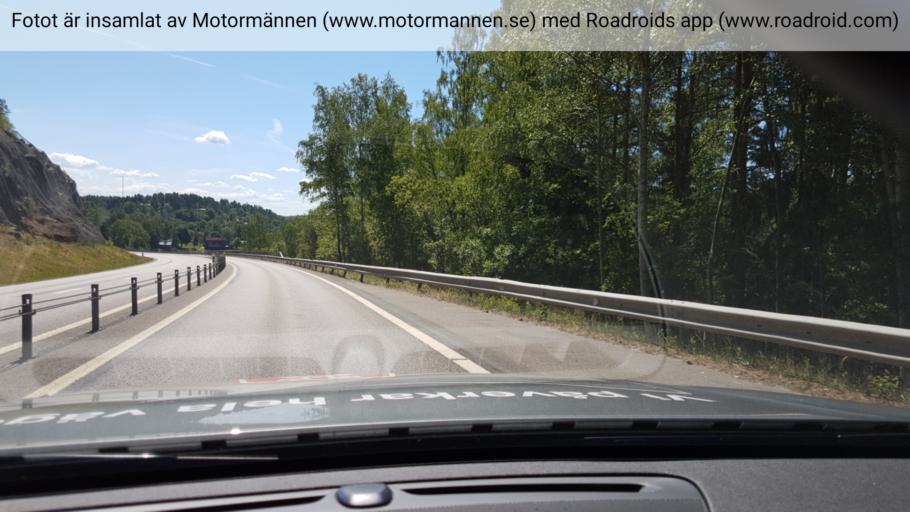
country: SE
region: OEstergoetland
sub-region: Norrkopings Kommun
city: Jursla
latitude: 58.7026
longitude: 16.1556
